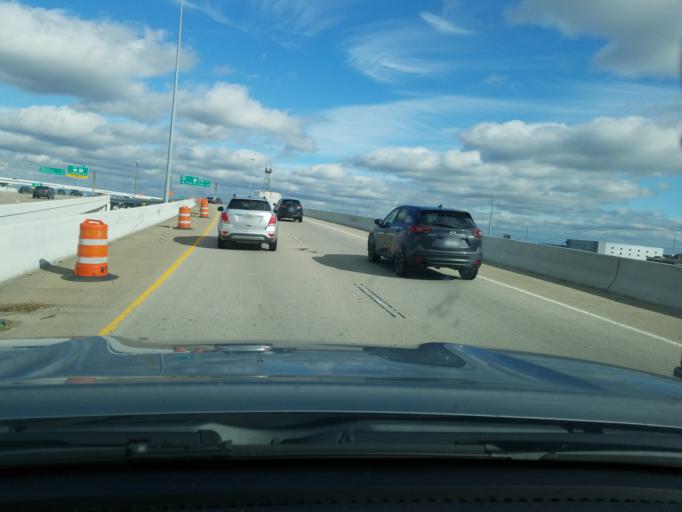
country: US
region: Texas
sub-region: Tarrant County
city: Fort Worth
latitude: 32.7444
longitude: -97.3262
